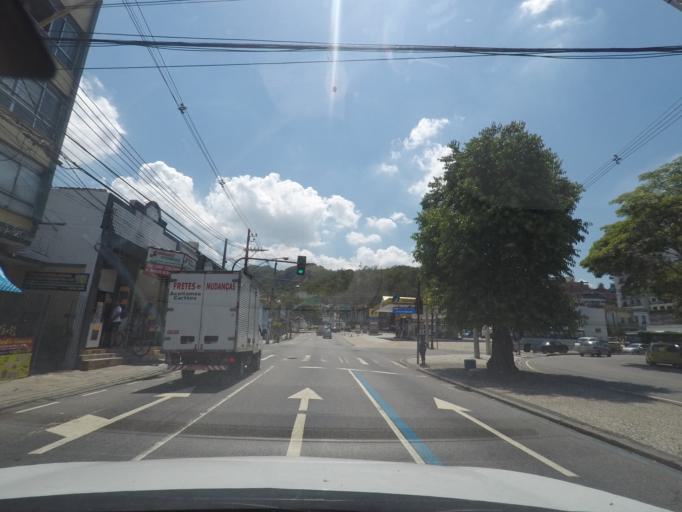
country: BR
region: Rio de Janeiro
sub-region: Rio De Janeiro
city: Rio de Janeiro
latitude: -22.9170
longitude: -43.2617
